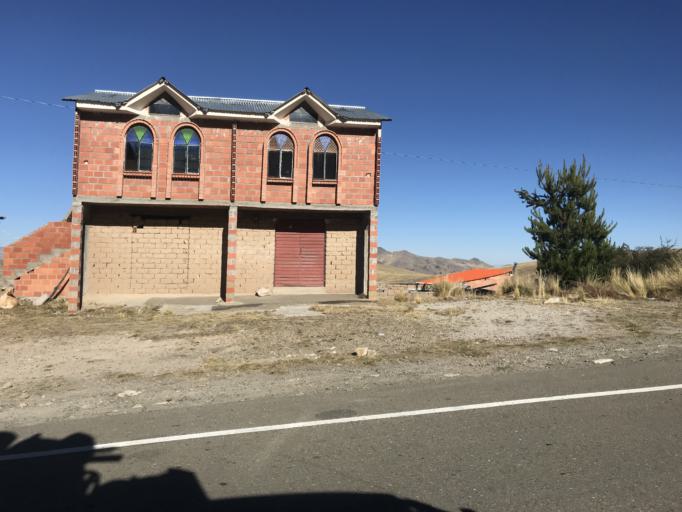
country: PE
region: Puno
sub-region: Yunguyo
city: Yunguyo
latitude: -16.1678
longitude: -68.9850
